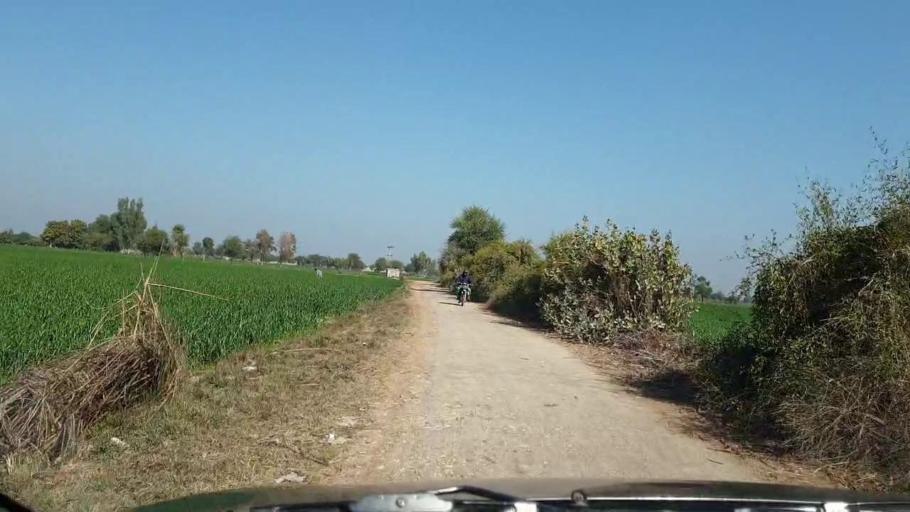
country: PK
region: Sindh
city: Sinjhoro
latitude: 25.9399
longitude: 68.7635
